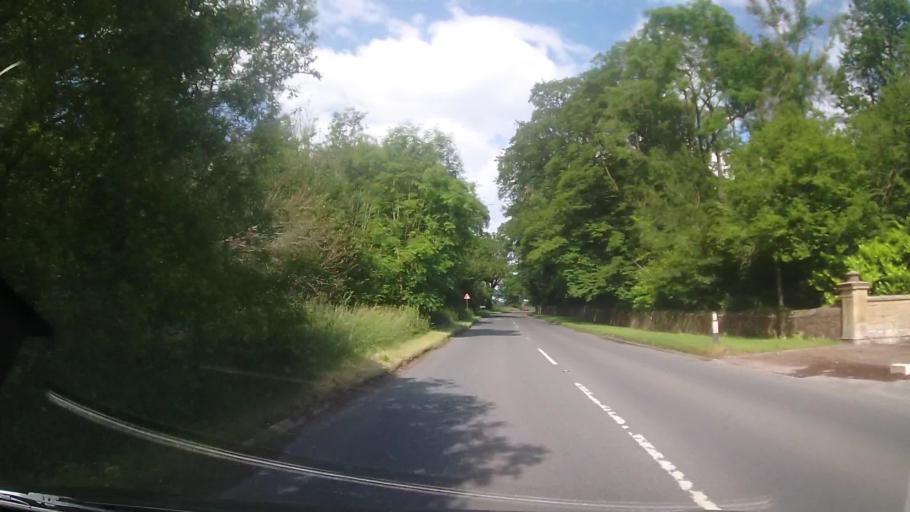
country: GB
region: England
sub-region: Shropshire
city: Whittington
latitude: 52.8819
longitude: -2.9886
